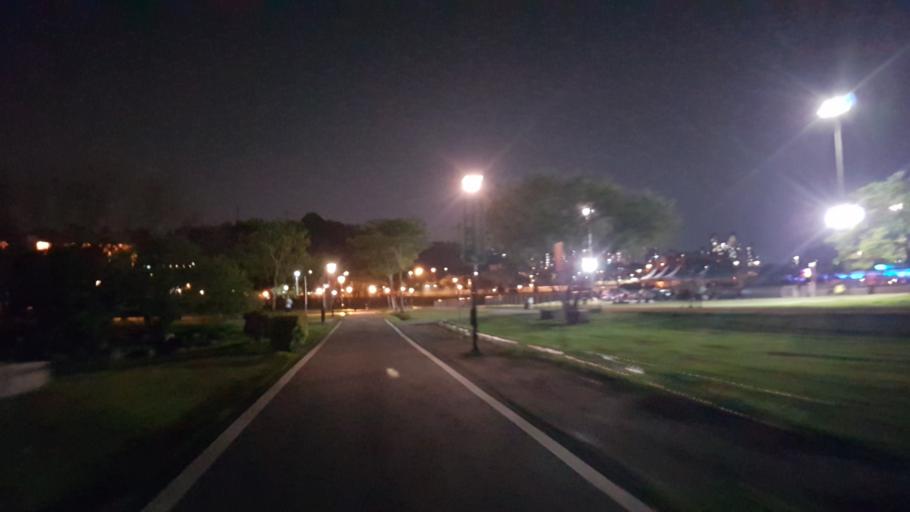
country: TW
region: Taipei
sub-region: Taipei
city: Banqiao
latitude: 24.9761
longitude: 121.5203
